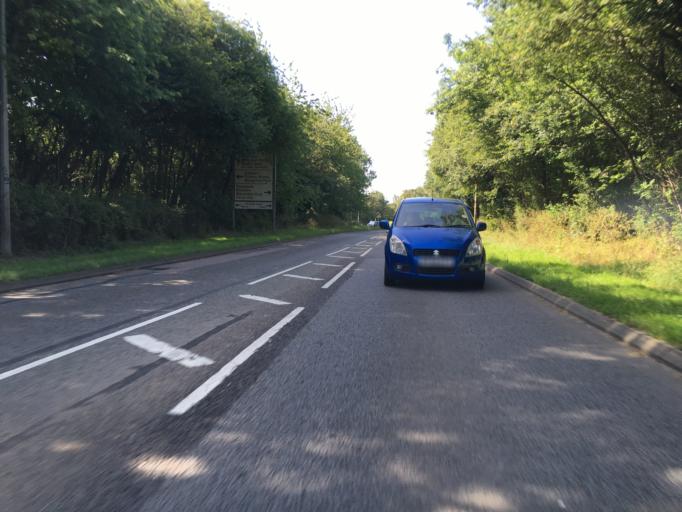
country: GB
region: England
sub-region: Milton Keynes
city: Simpson
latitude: 52.0213
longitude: -0.7022
